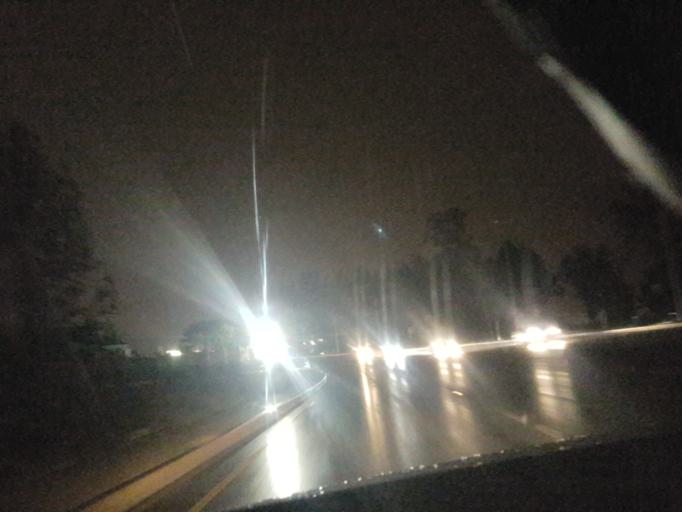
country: ZA
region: Gauteng
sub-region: City of Johannesburg Metropolitan Municipality
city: Diepsloot
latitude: -25.9958
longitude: 27.9829
